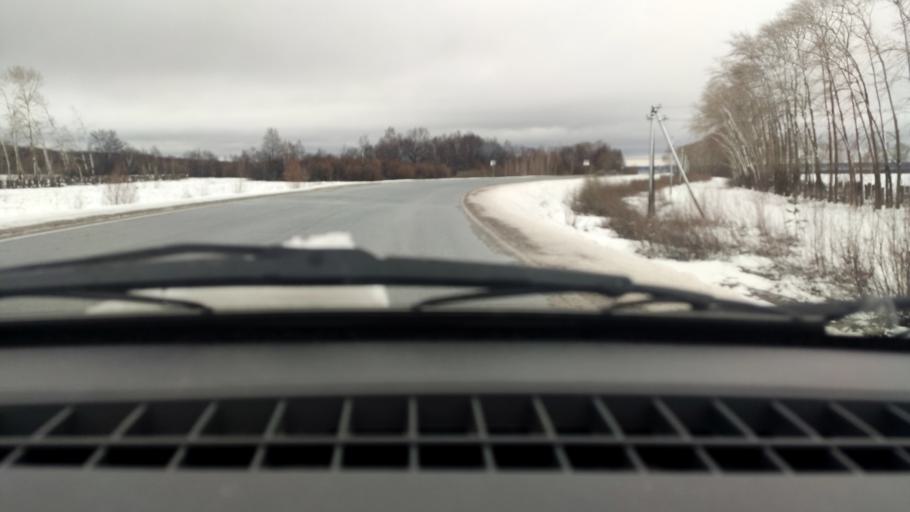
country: RU
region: Bashkortostan
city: Kushnarenkovo
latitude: 55.0600
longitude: 55.1843
